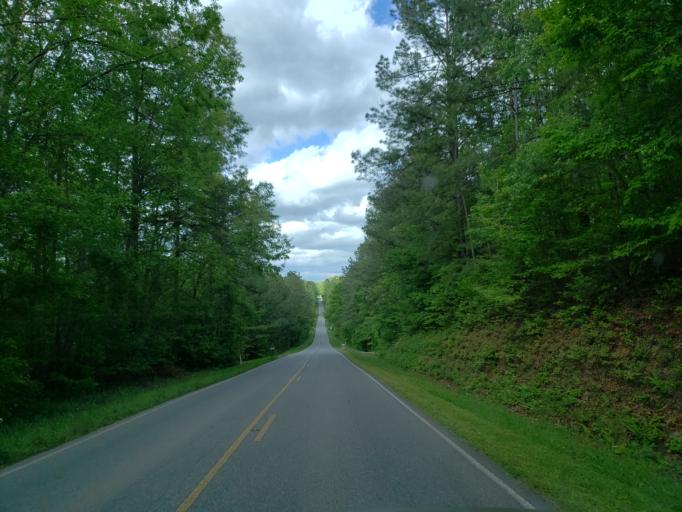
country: US
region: Georgia
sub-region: Haralson County
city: Tallapoosa
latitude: 33.6873
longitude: -85.3699
